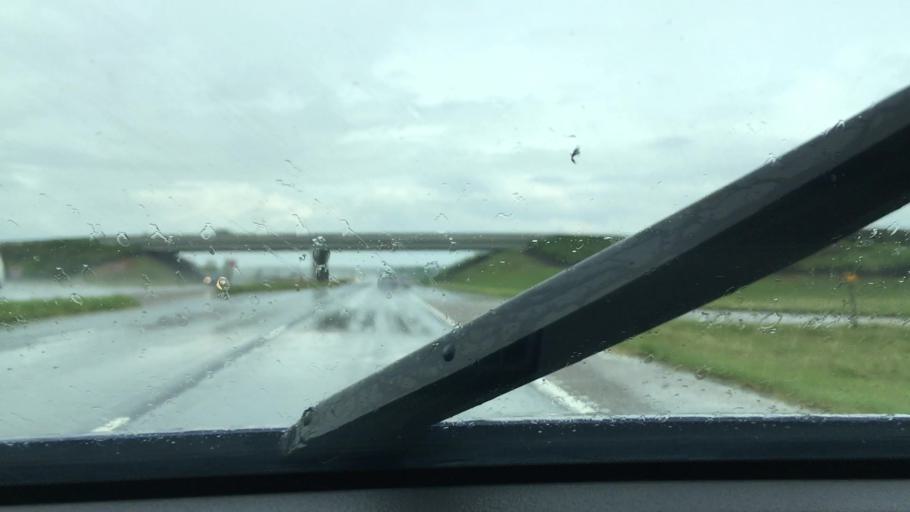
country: US
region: South Carolina
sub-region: Sumter County
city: Oakland
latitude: 33.9537
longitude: -80.4921
